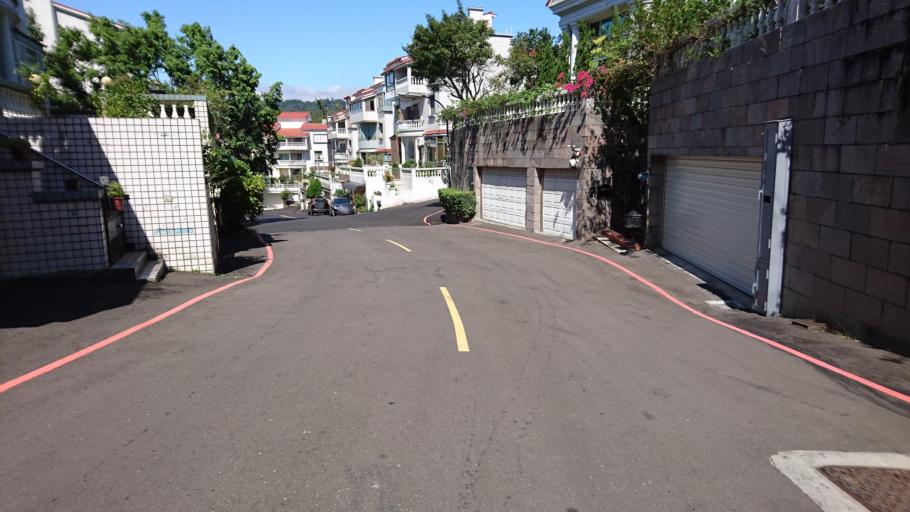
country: TW
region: Taiwan
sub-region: Hsinchu
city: Zhubei
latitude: 24.7897
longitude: 121.0769
